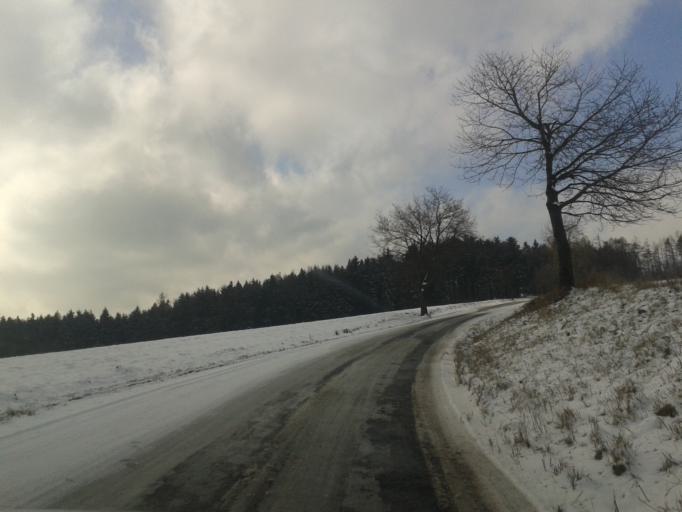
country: CZ
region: Olomoucky
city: Horni Stepanov
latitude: 49.5361
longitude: 16.8309
